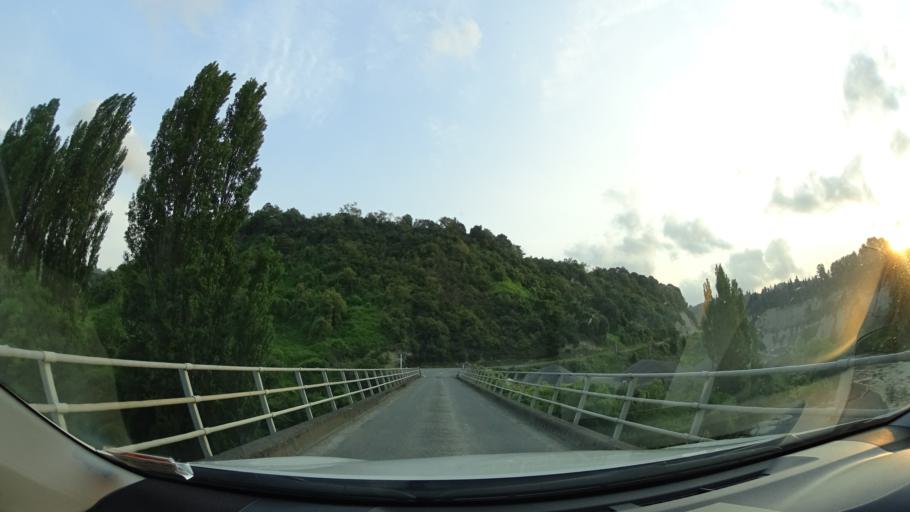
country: NZ
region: Manawatu-Wanganui
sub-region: Ruapehu District
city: Waiouru
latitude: -39.7542
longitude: 175.8355
